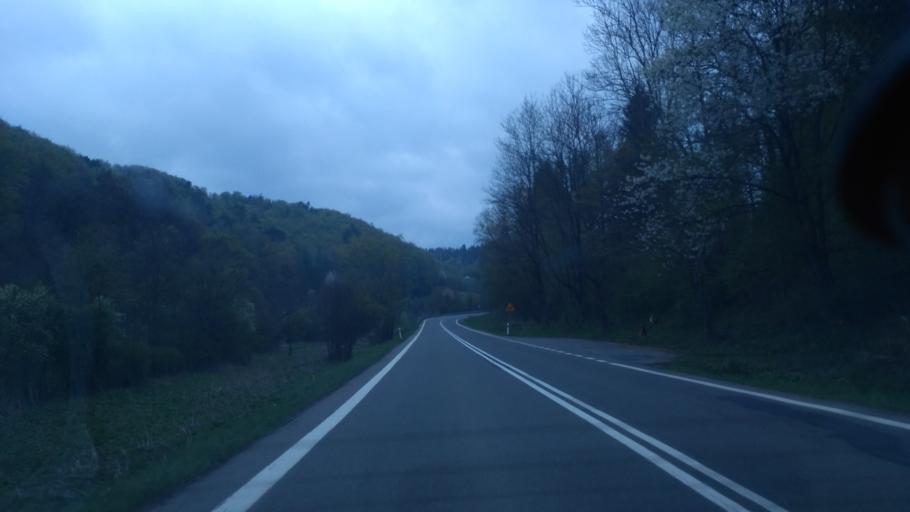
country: PL
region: Subcarpathian Voivodeship
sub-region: Powiat sanocki
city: Zagorz
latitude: 49.5394
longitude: 22.3035
